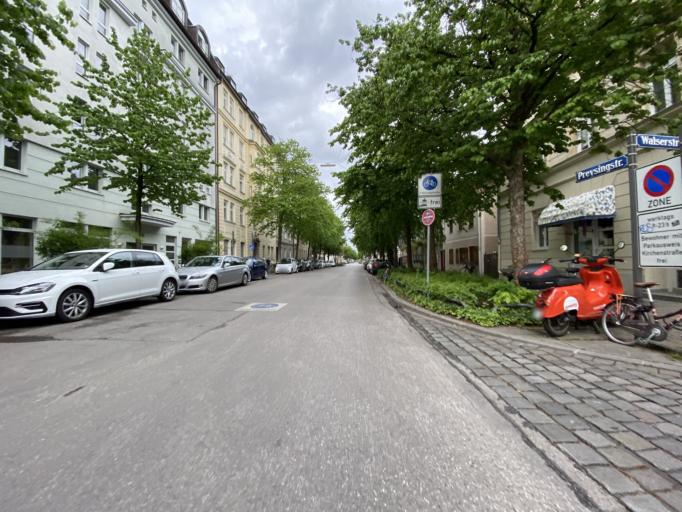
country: DE
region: Bavaria
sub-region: Upper Bavaria
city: Munich
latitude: 48.1324
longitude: 11.5992
